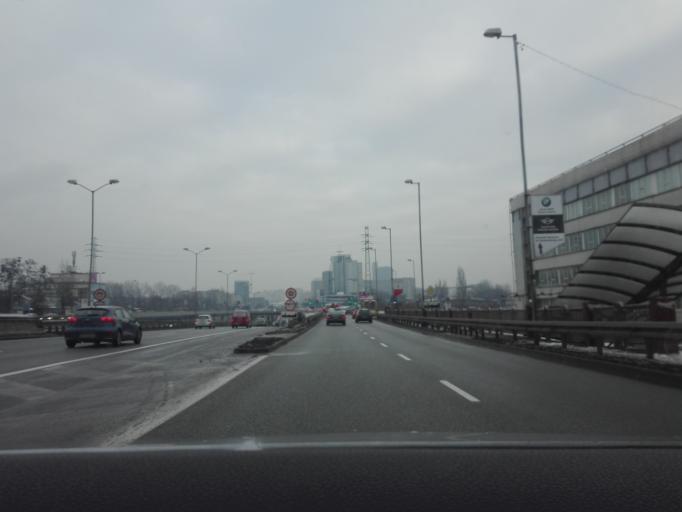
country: PL
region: Silesian Voivodeship
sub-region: Katowice
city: Katowice
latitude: 50.2680
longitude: 19.0078
